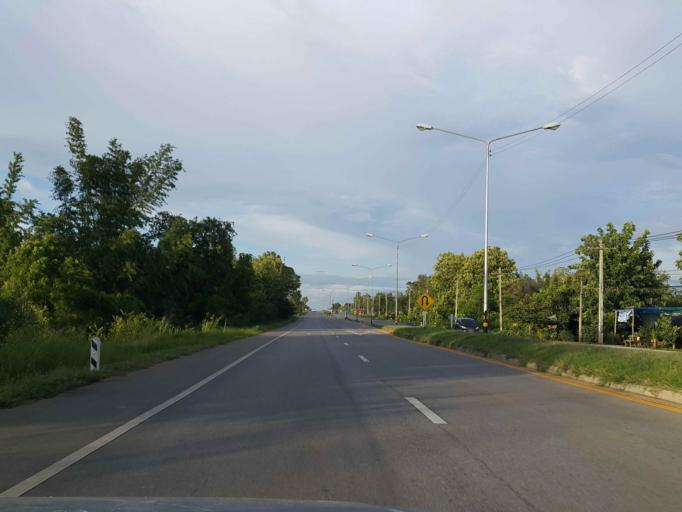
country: TH
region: Sukhothai
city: Ban Dan Lan Hoi
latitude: 16.9304
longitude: 99.4176
